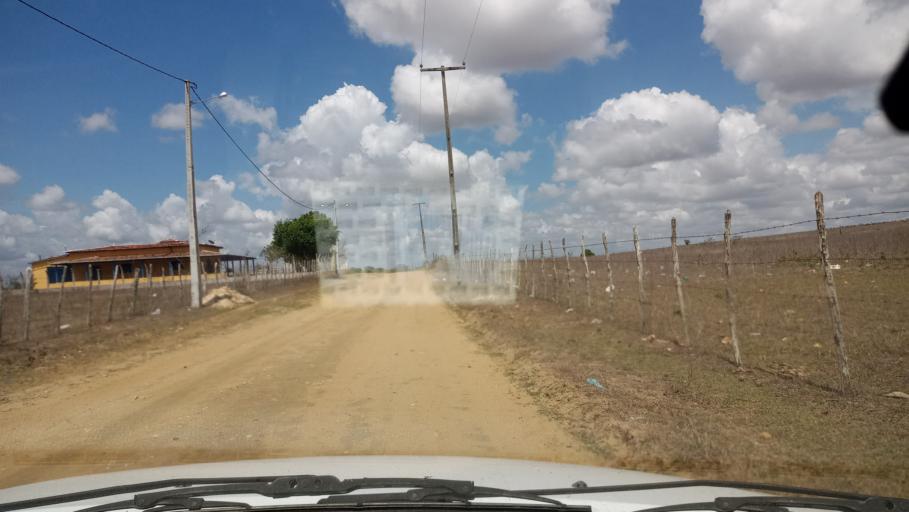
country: BR
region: Rio Grande do Norte
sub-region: Santo Antonio
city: Santo Antonio
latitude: -6.3468
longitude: -35.3787
